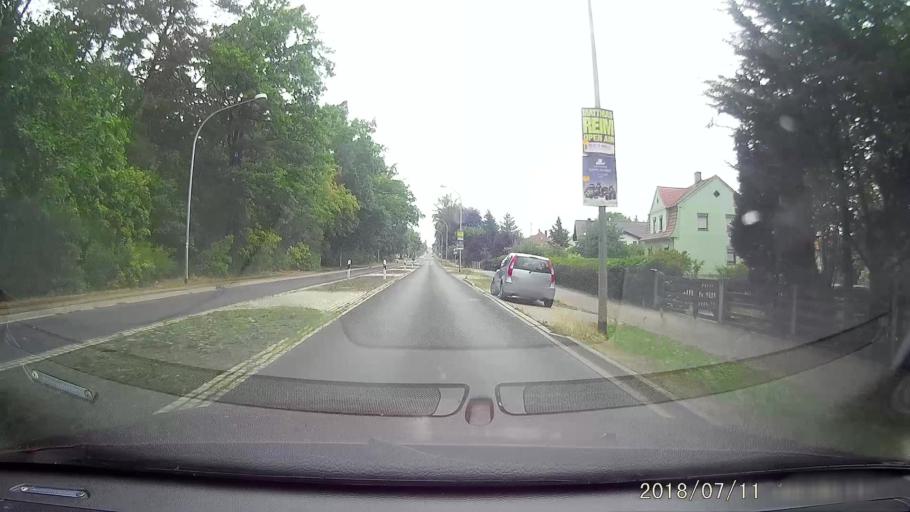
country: DE
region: Saxony
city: Niesky
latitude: 51.2815
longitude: 14.8189
